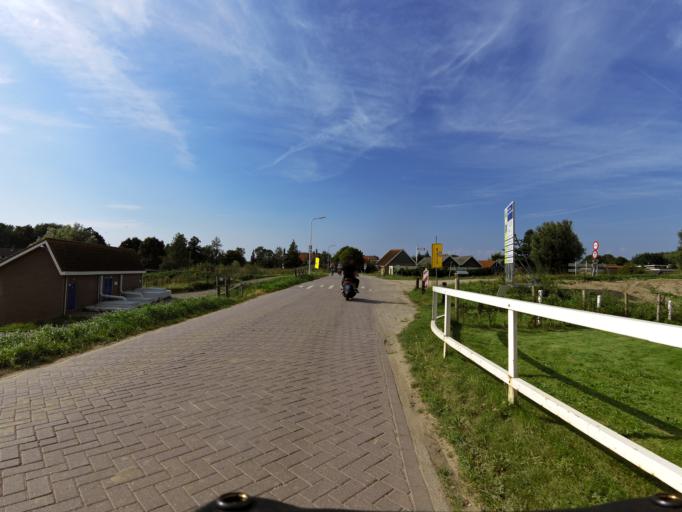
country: NL
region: South Holland
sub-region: Gemeente Zwijndrecht
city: Heerjansdam
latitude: 51.8025
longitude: 4.5750
